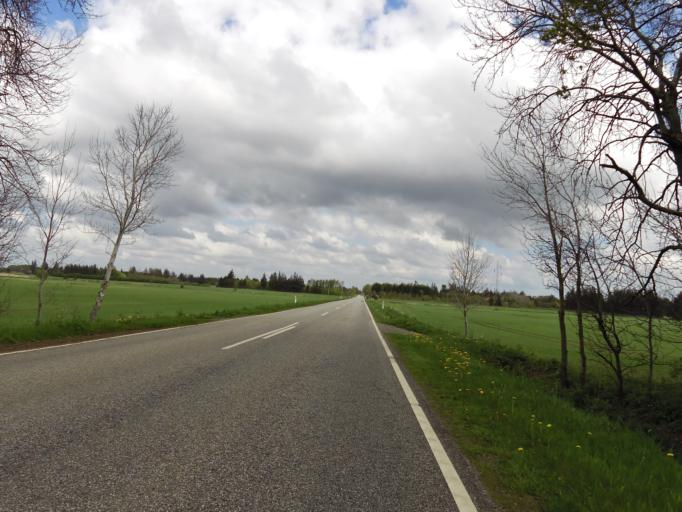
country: DK
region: South Denmark
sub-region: Haderslev Kommune
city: Gram
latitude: 55.2539
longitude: 8.9836
